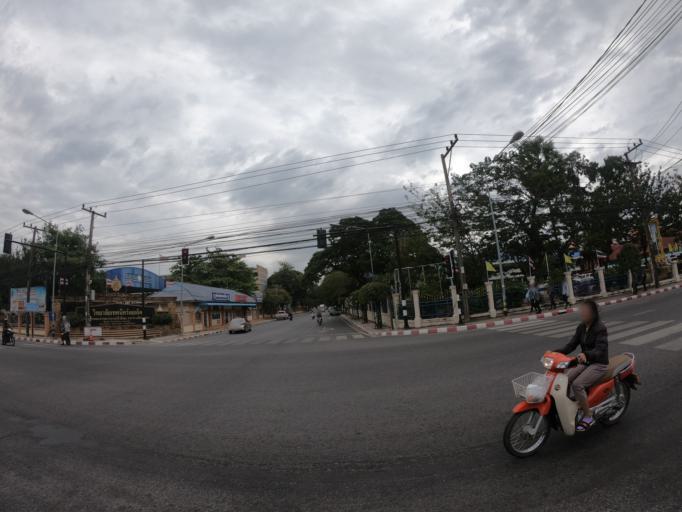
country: TH
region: Roi Et
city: Roi Et
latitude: 16.0537
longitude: 103.6551
